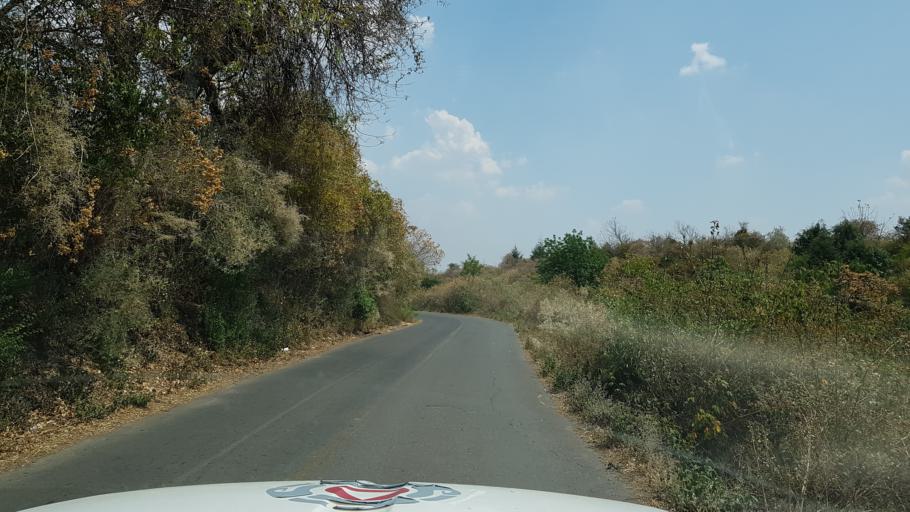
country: MX
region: Morelos
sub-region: Yecapixtla
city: Texcala
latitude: 18.9204
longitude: -98.8120
